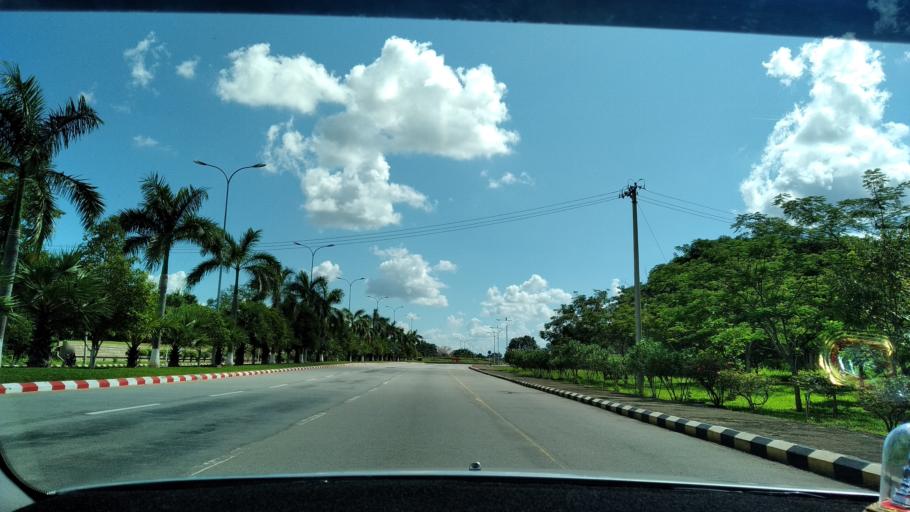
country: MM
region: Mandalay
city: Nay Pyi Taw
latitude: 19.7706
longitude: 96.1419
